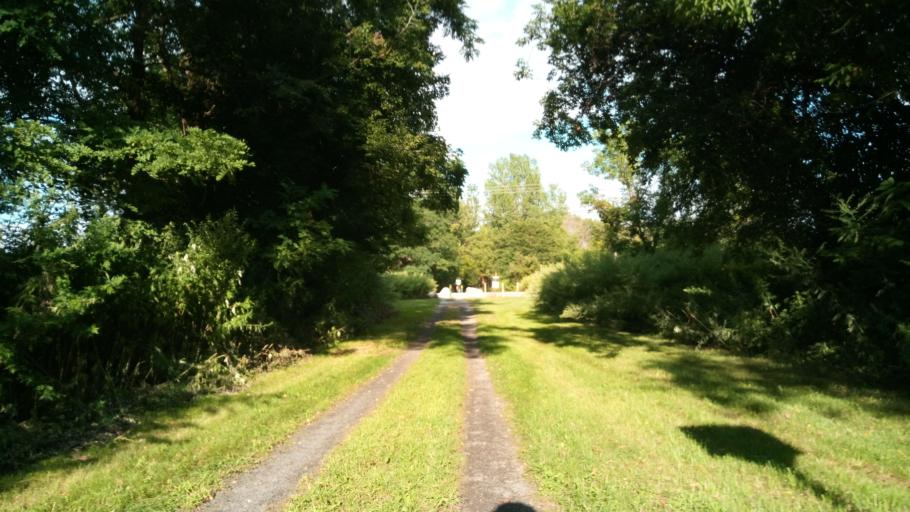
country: US
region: New York
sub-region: Monroe County
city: Honeoye Falls
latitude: 42.9923
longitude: -77.5267
